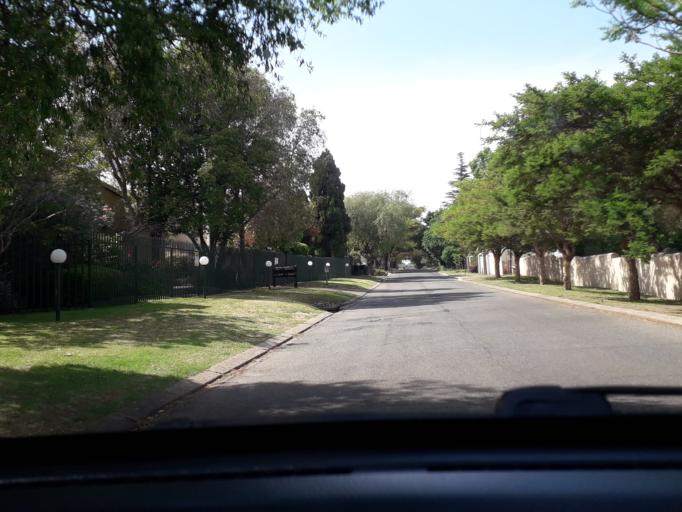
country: ZA
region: Gauteng
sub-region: City of Johannesburg Metropolitan Municipality
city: Diepsloot
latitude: -26.0417
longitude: 28.0092
